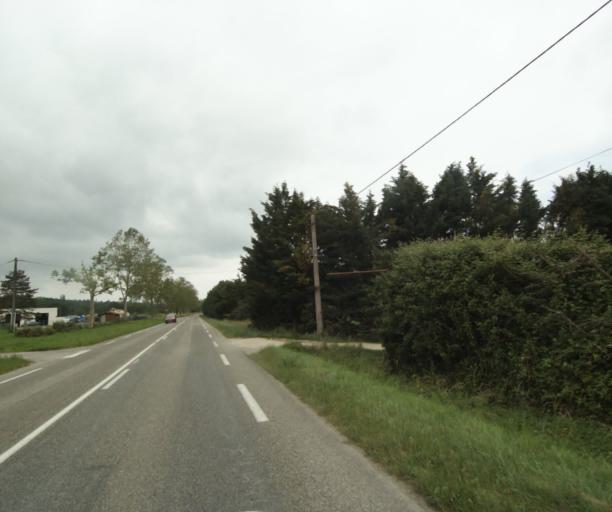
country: FR
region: Midi-Pyrenees
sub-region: Departement du Tarn-et-Garonne
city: Saint-Nauphary
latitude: 43.9746
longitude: 1.4135
